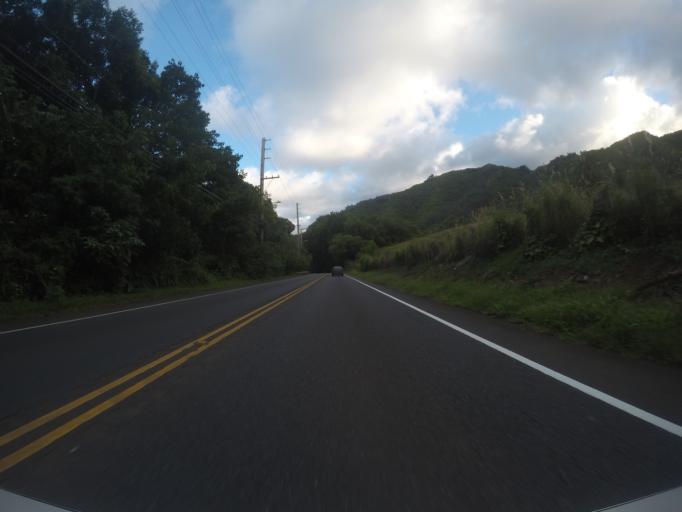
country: US
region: Hawaii
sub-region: Honolulu County
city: Ka'a'awa
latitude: 21.5063
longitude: -157.8559
